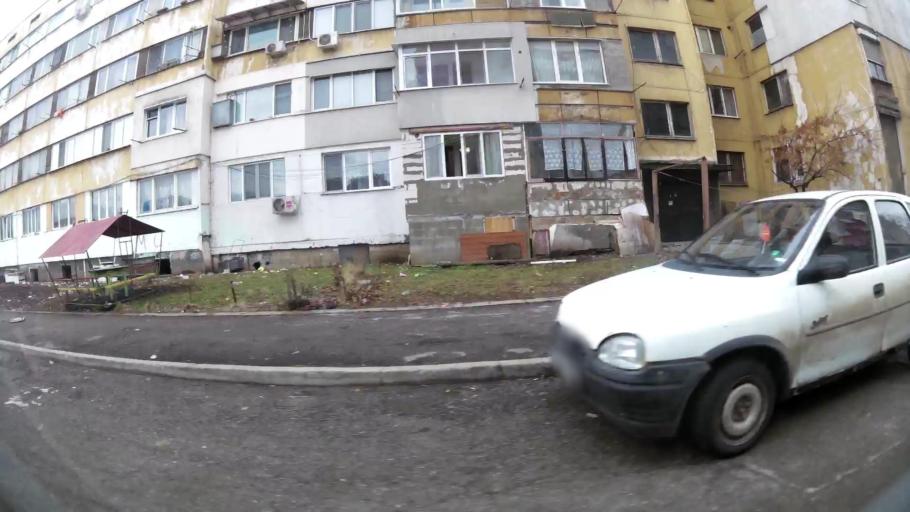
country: BG
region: Sofiya
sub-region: Obshtina Bozhurishte
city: Bozhurishte
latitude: 42.7295
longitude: 23.2485
